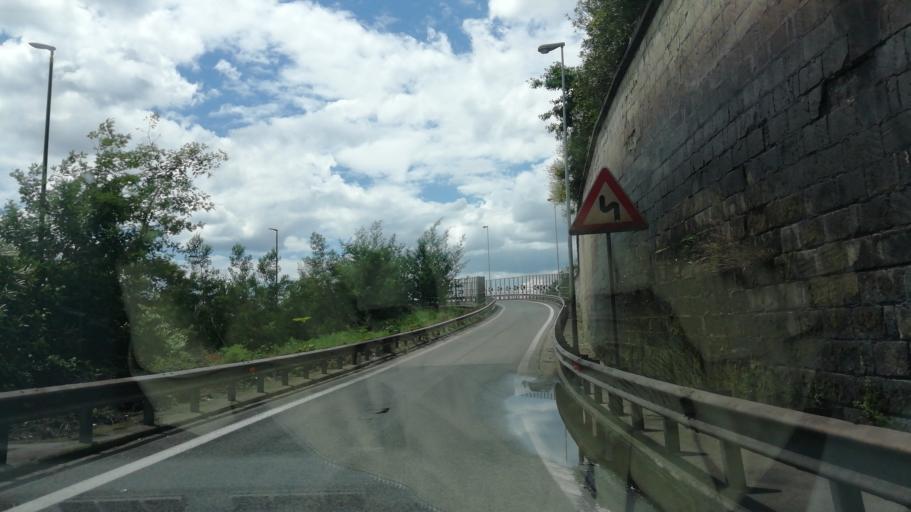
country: IT
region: Campania
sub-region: Provincia di Napoli
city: Napoli
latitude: 40.8479
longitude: 14.2125
